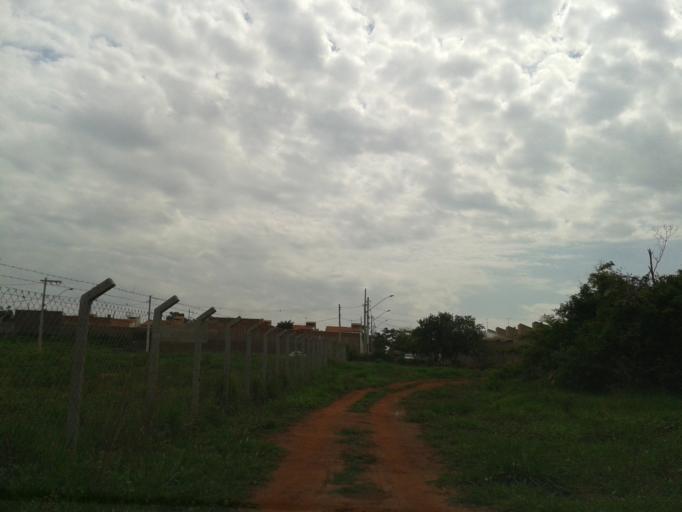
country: BR
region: Minas Gerais
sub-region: Ituiutaba
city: Ituiutaba
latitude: -18.9825
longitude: -49.4423
